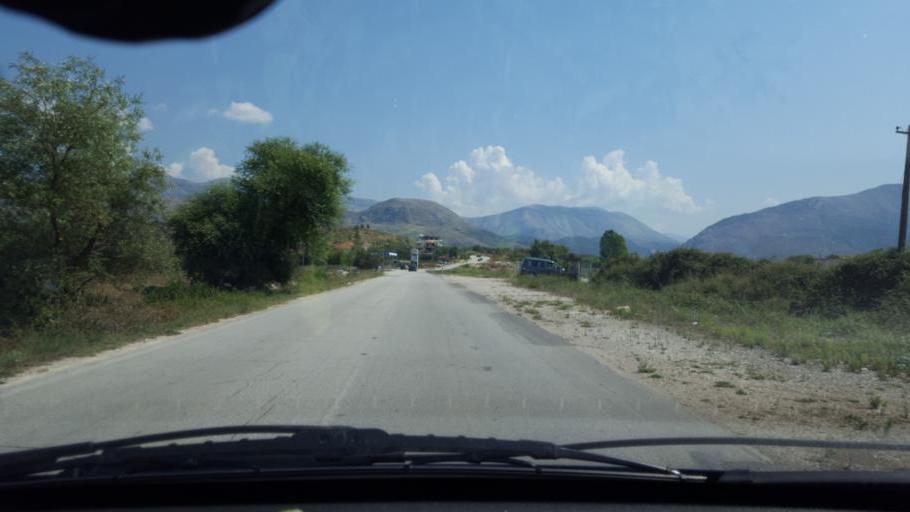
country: AL
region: Vlore
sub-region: Rrethi i Delvines
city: Finiq
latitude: 39.8962
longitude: 20.0726
